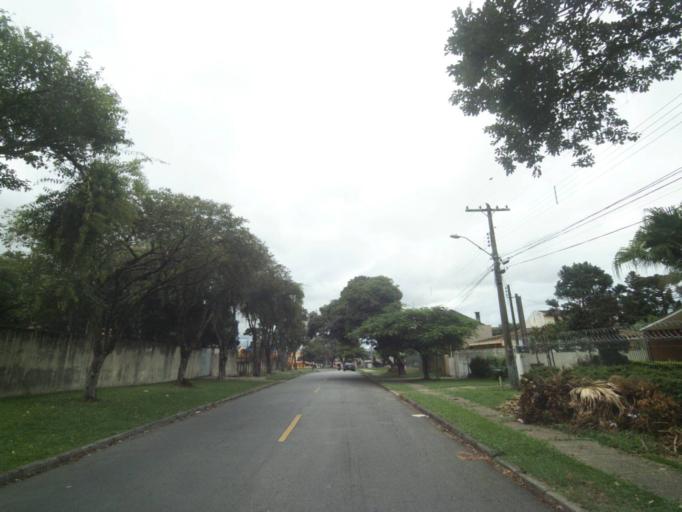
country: BR
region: Parana
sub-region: Curitiba
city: Curitiba
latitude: -25.4751
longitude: -49.2704
